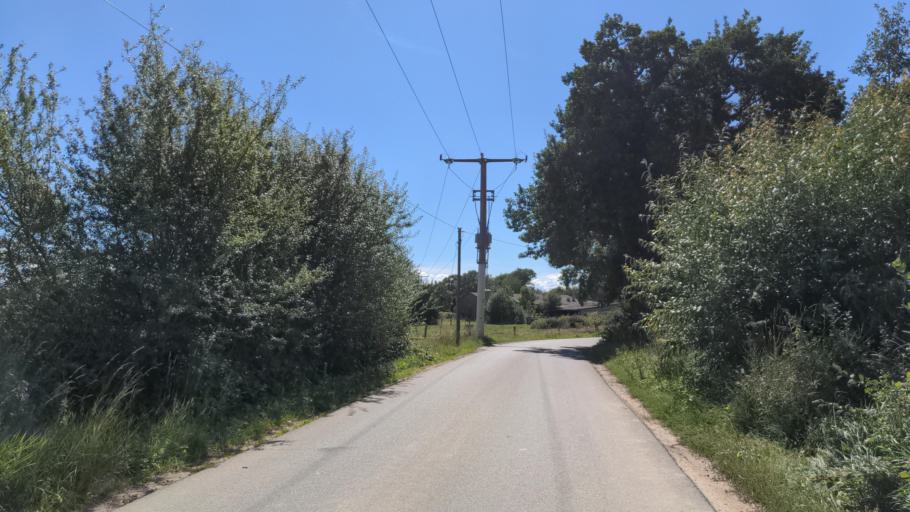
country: DE
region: Schleswig-Holstein
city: Beschendorf
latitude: 54.1853
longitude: 10.8224
